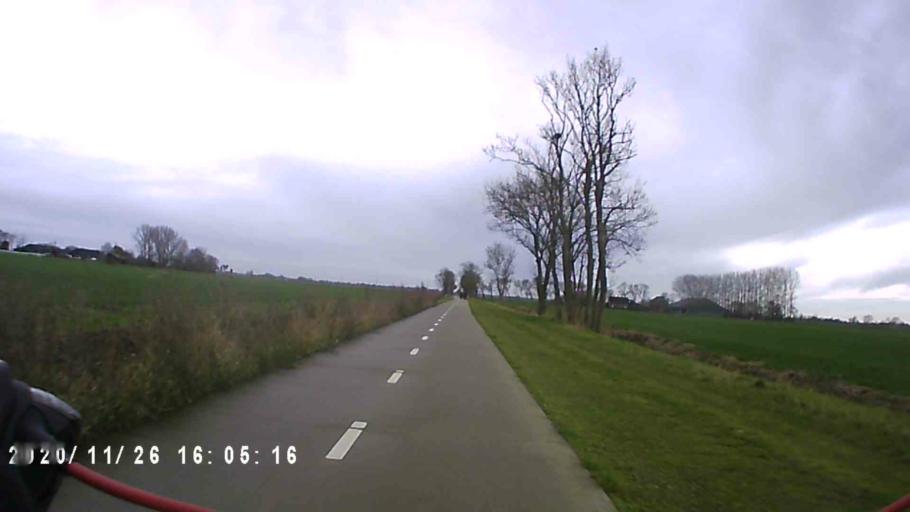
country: NL
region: Groningen
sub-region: Gemeente Bedum
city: Bedum
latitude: 53.2671
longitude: 6.6752
